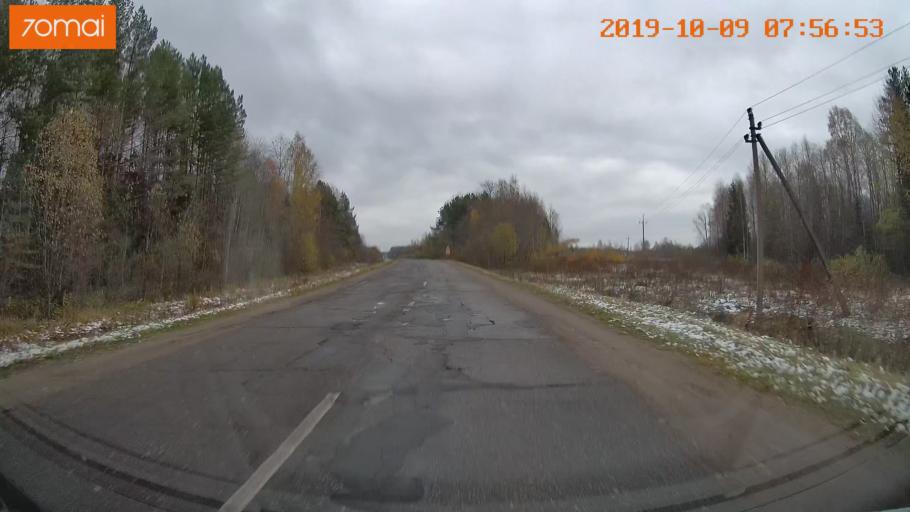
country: RU
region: Jaroslavl
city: Kukoboy
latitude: 58.6971
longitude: 39.9424
